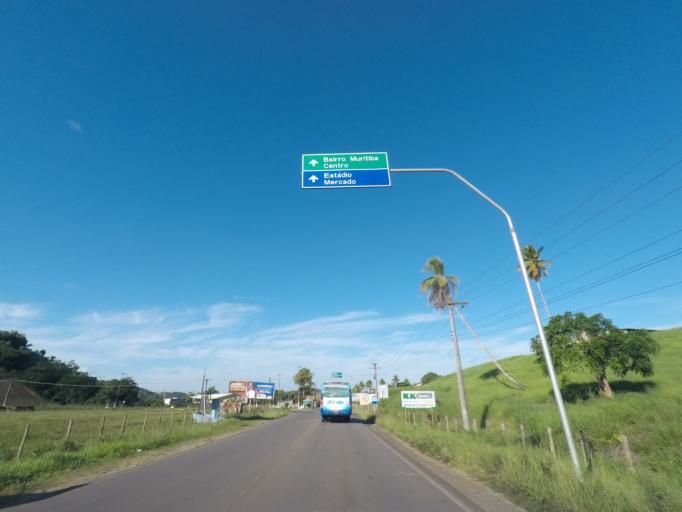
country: BR
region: Bahia
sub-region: Nazare
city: Nazare
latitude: -13.0437
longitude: -39.0055
